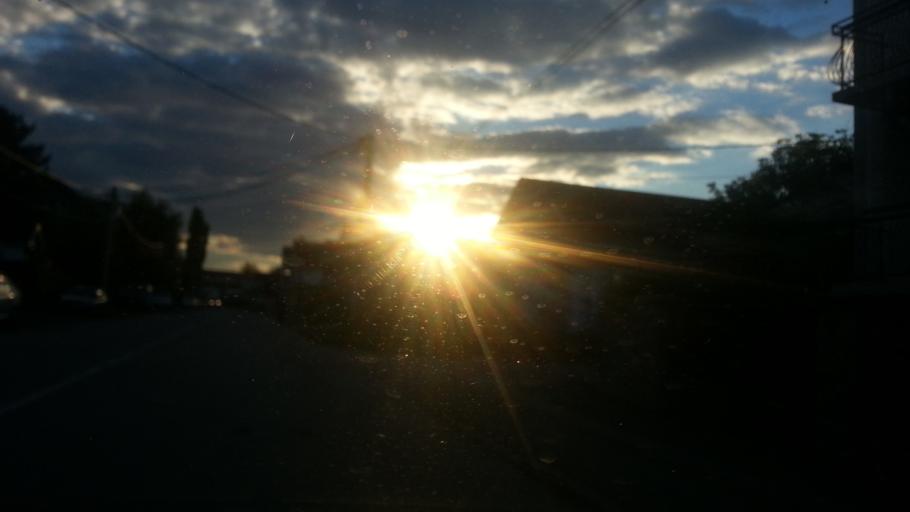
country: RS
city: Novi Banovci
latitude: 44.9063
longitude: 20.2873
